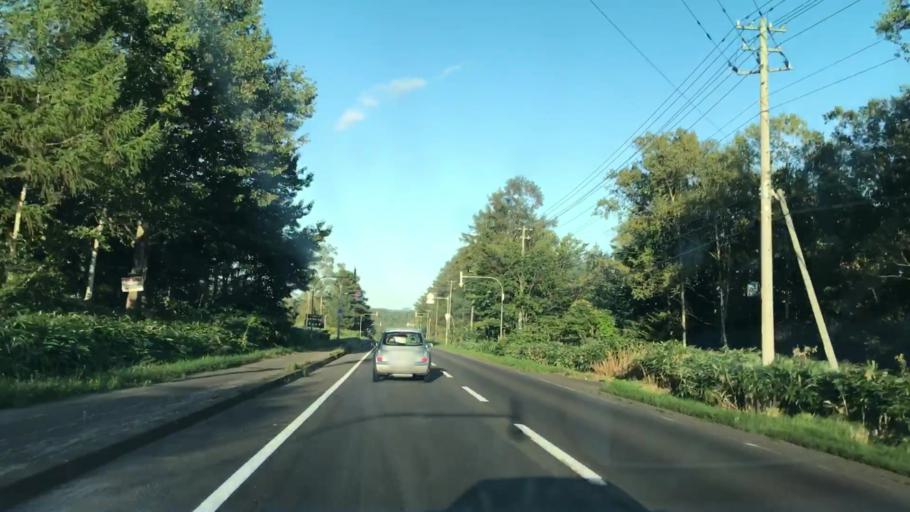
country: JP
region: Hokkaido
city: Niseko Town
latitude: 42.7528
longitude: 140.9091
